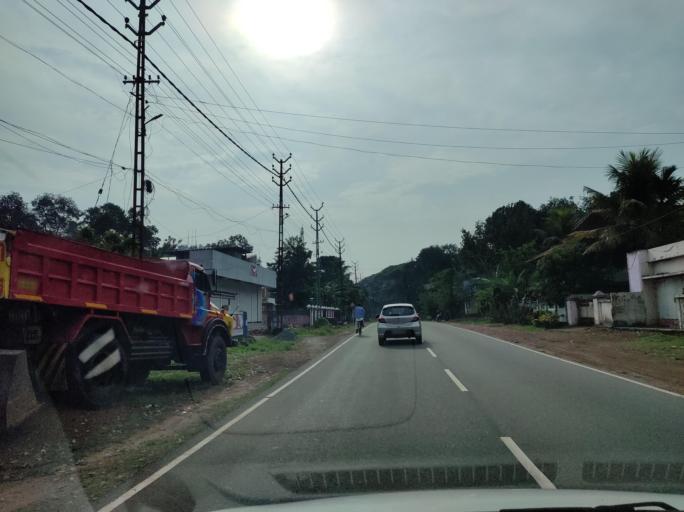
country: IN
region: Kerala
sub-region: Alappuzha
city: Kattanam
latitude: 9.1762
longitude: 76.5713
